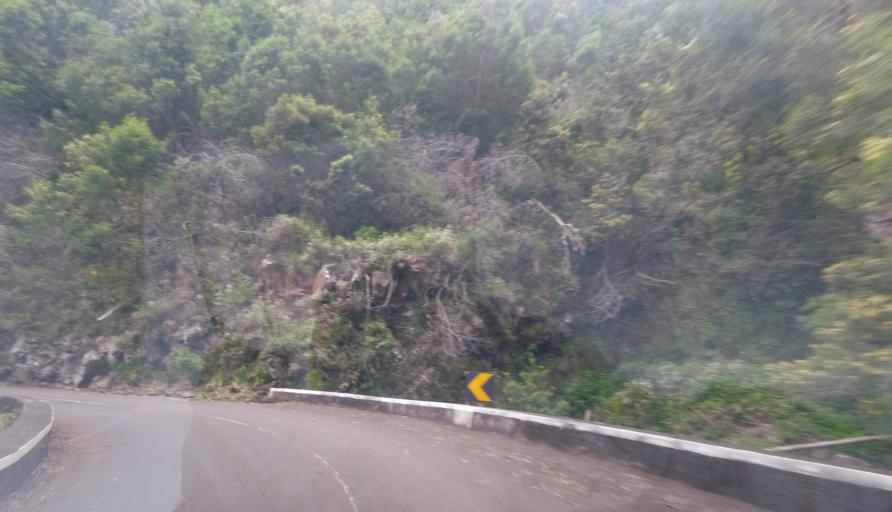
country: PT
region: Madeira
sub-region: Funchal
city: Nossa Senhora do Monte
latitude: 32.6904
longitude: -16.8893
